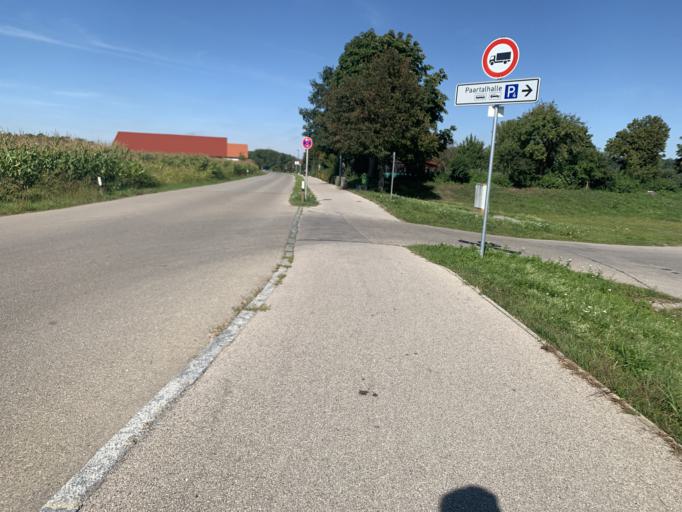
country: DE
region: Bavaria
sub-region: Swabia
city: Kissing
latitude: 48.3076
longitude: 10.9809
